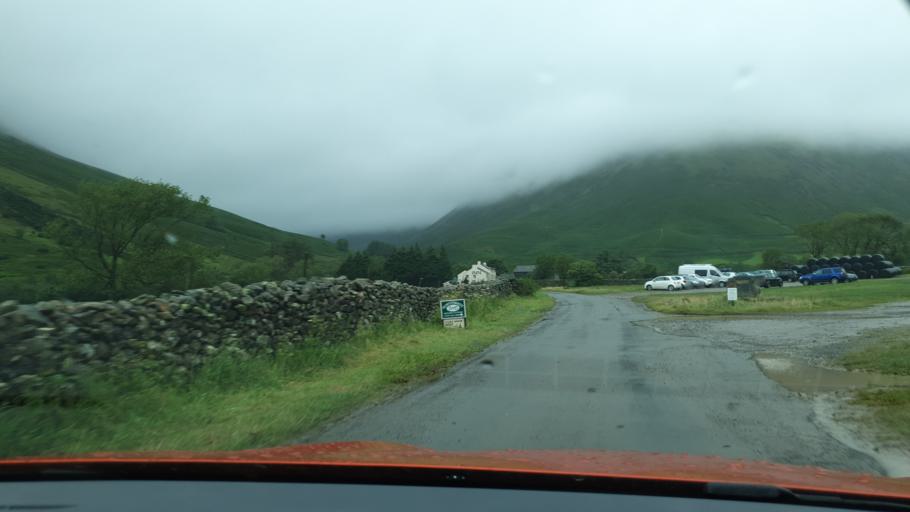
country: GB
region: England
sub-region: Cumbria
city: Keswick
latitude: 54.4648
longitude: -3.2565
